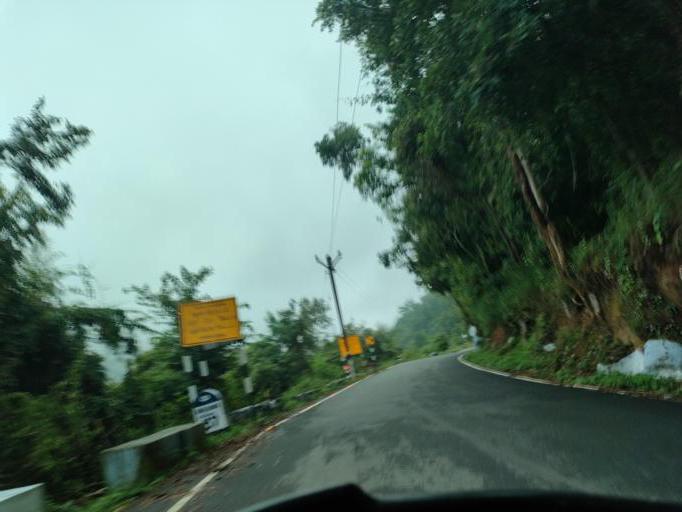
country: IN
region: Tamil Nadu
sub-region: Dindigul
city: Ayakudi
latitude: 10.3603
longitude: 77.5526
